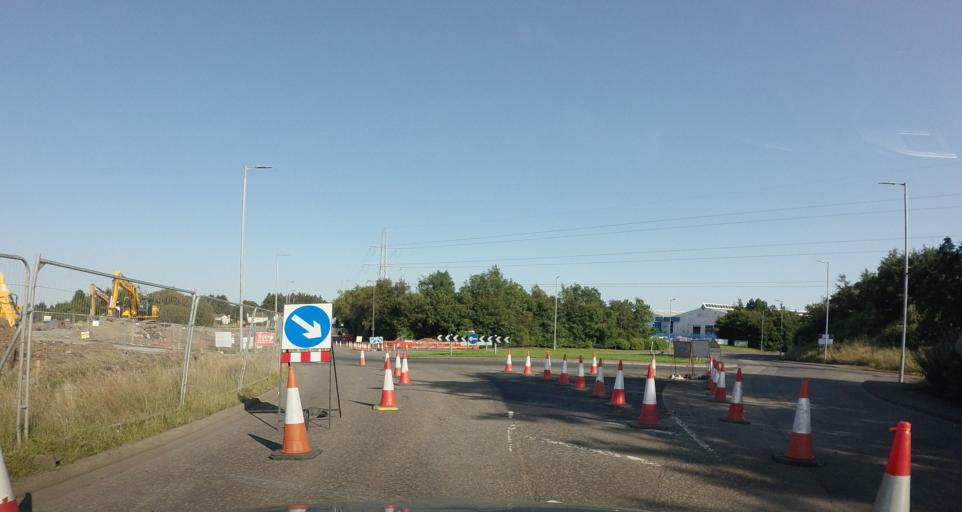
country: GB
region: Scotland
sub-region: South Lanarkshire
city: East Kilbride
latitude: 55.7423
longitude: -4.1633
